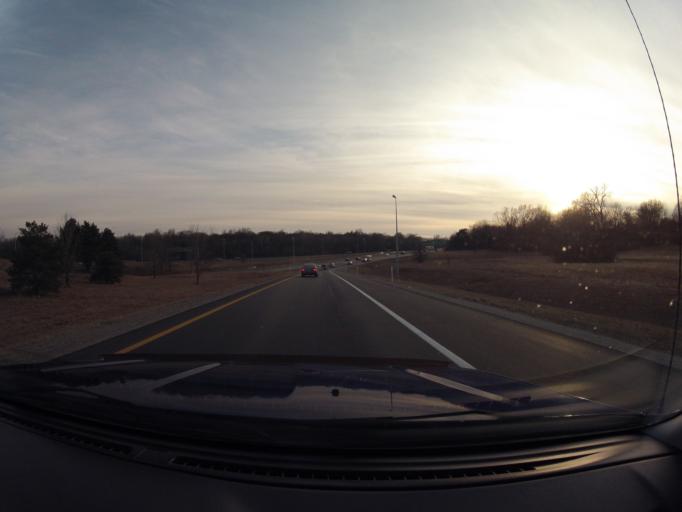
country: US
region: Kansas
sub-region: Shawnee County
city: Topeka
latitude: 39.0674
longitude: -95.7324
